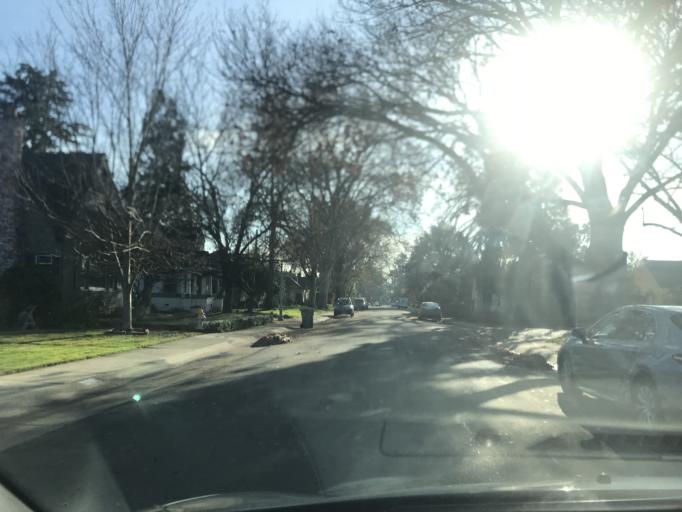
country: US
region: California
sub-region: Sacramento County
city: Sacramento
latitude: 38.5600
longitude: -121.4973
